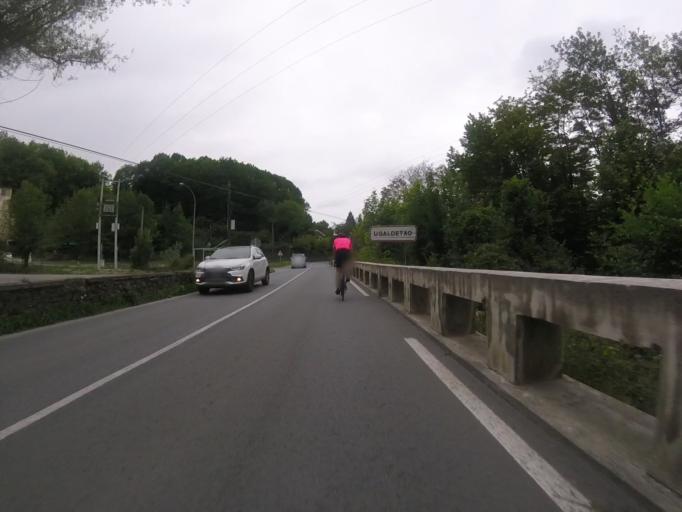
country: ES
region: Basque Country
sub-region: Provincia de Guipuzcoa
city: Errenteria
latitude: 43.2976
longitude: -1.8751
